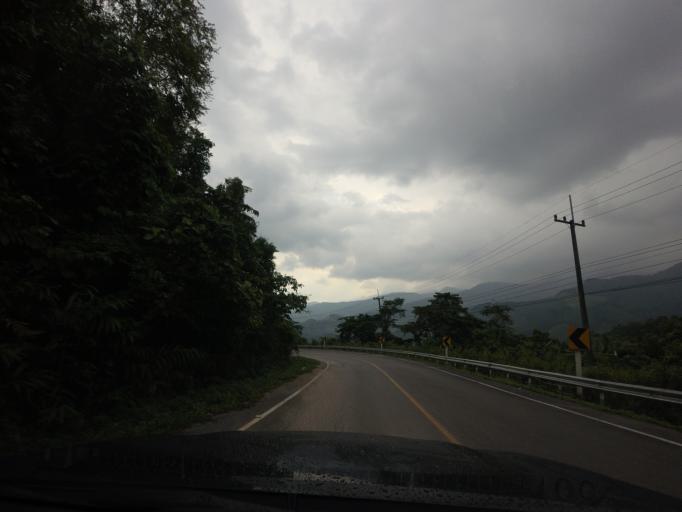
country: TH
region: Nan
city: Bo Kluea
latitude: 19.1691
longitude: 101.1435
